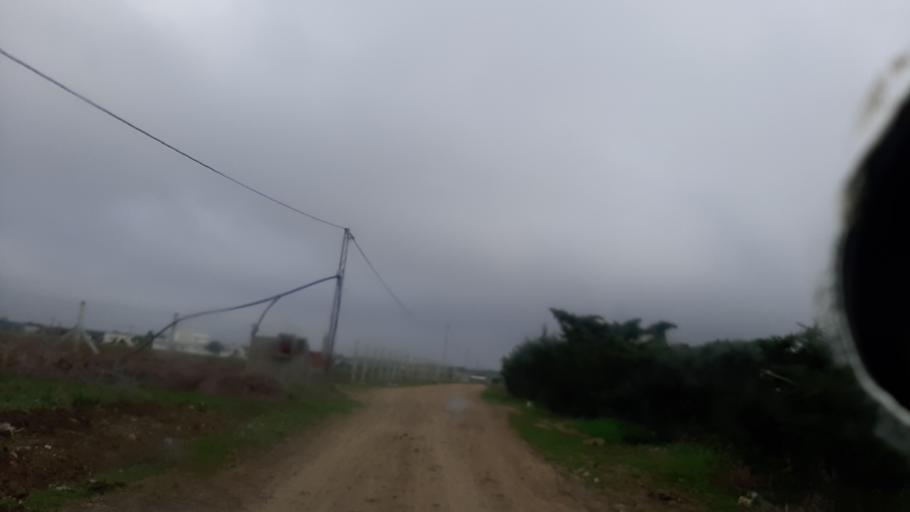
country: TN
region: Nabul
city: Qulaybiyah
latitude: 36.8324
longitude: 11.0348
